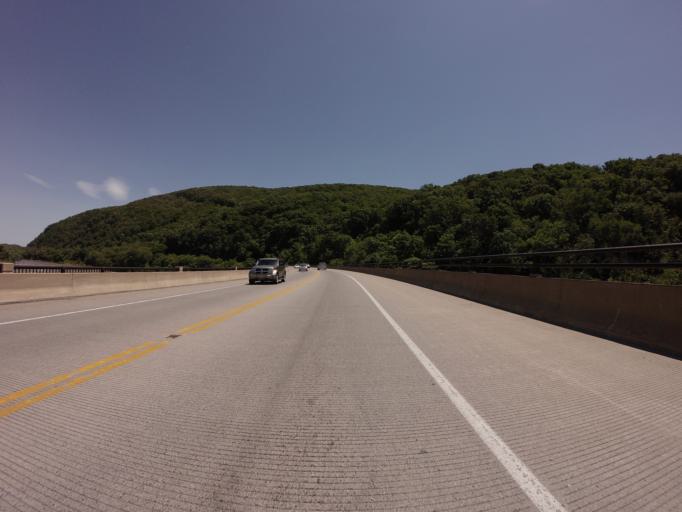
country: US
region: West Virginia
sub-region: Jefferson County
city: Bolivar
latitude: 39.3198
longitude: -77.7415
